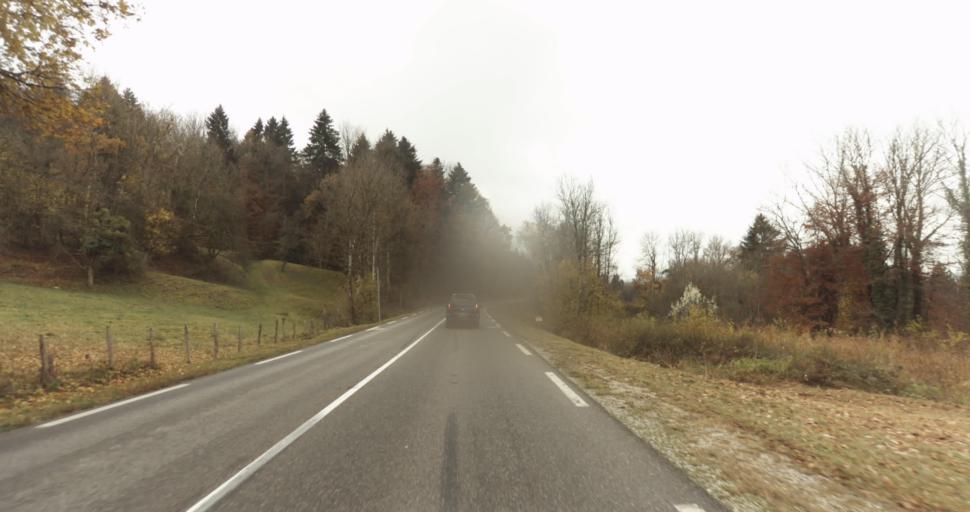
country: FR
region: Rhone-Alpes
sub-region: Departement de la Haute-Savoie
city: Evires
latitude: 46.0149
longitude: 6.2129
